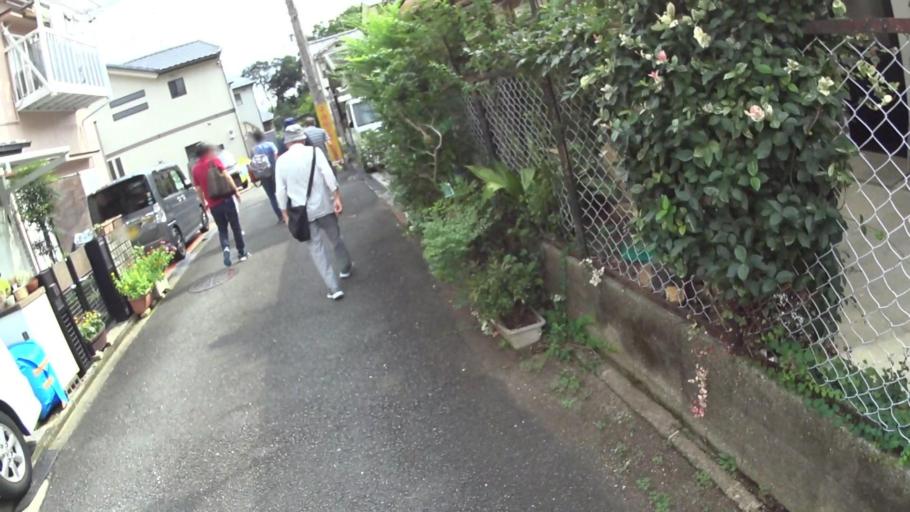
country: JP
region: Kyoto
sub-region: Kyoto-shi
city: Kamigyo-ku
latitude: 35.0518
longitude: 135.7386
